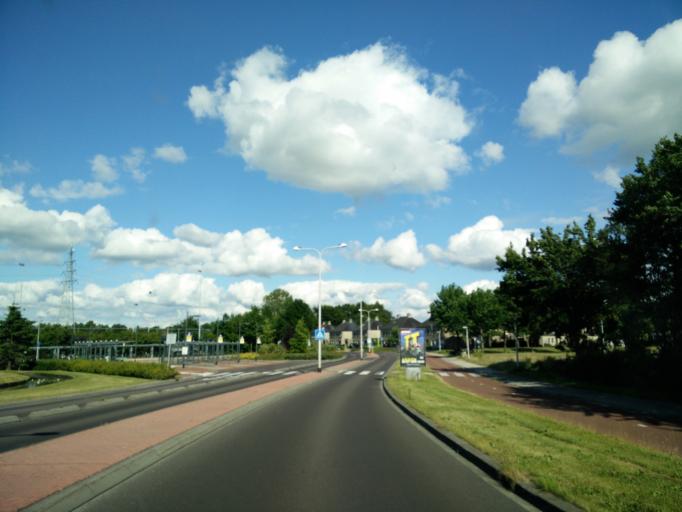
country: NL
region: Drenthe
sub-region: Gemeente Assen
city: Assen
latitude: 53.0177
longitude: 6.5716
